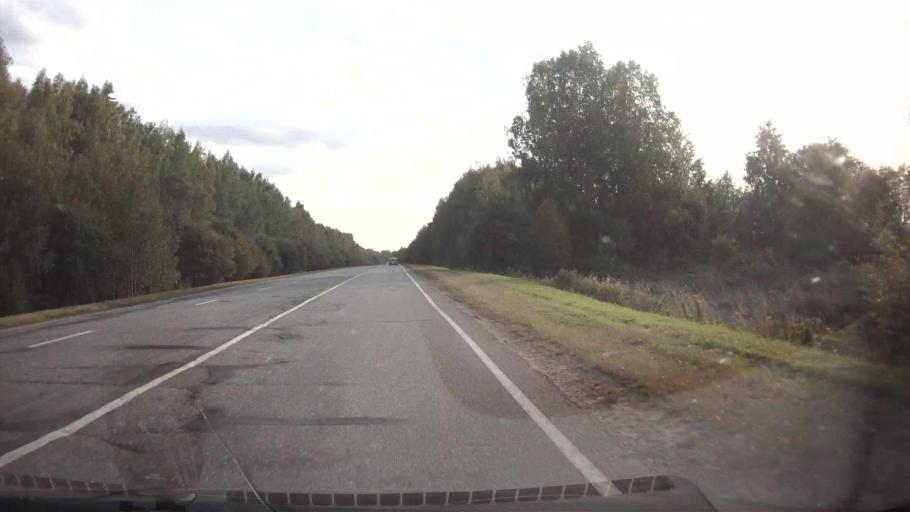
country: RU
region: Mariy-El
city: Sovetskiy
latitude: 56.8035
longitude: 48.6910
